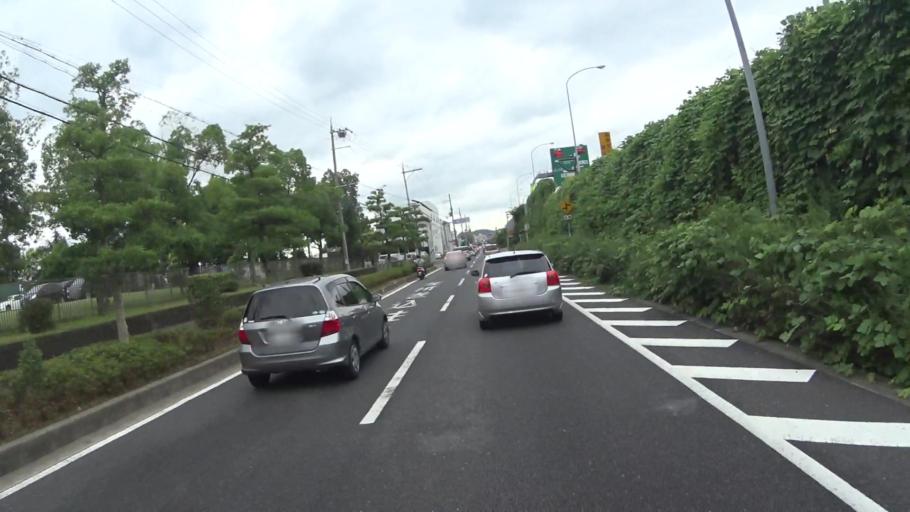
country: JP
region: Kyoto
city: Muko
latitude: 34.9231
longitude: 135.7109
